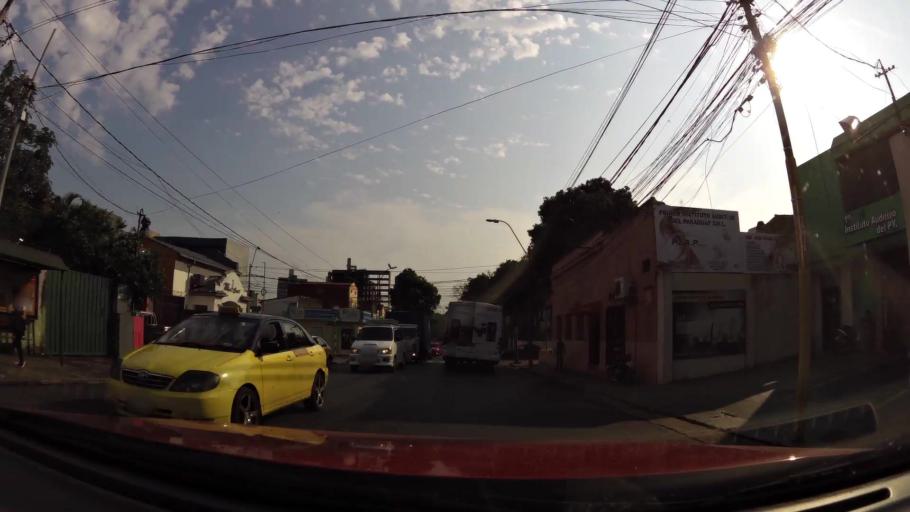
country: PY
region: Asuncion
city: Asuncion
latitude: -25.2909
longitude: -57.6202
